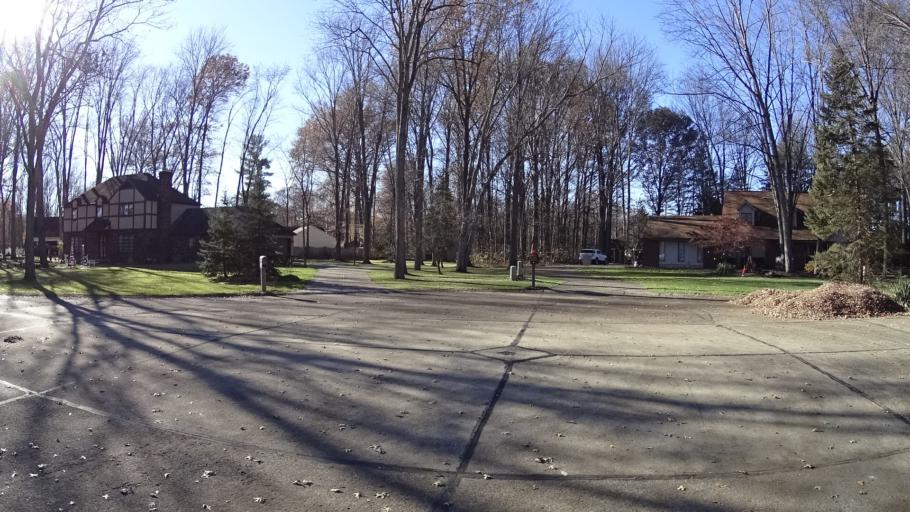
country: US
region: Ohio
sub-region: Lorain County
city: Elyria
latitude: 41.3391
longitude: -82.0827
